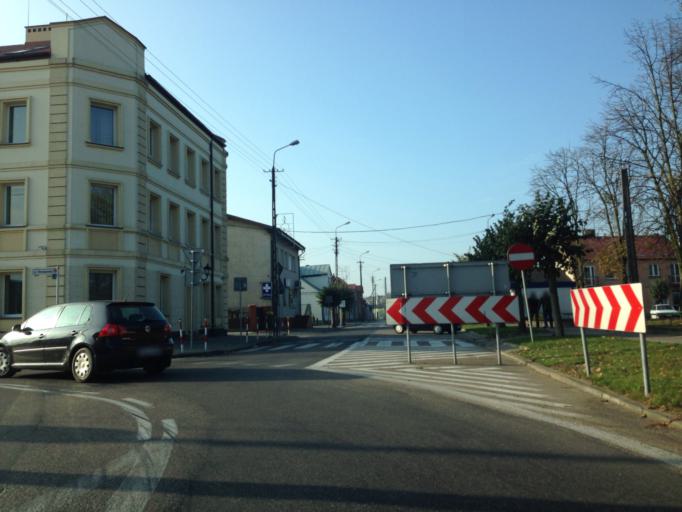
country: PL
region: Masovian Voivodeship
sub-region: Powiat zurominski
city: Biezun
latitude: 52.9617
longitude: 19.8911
